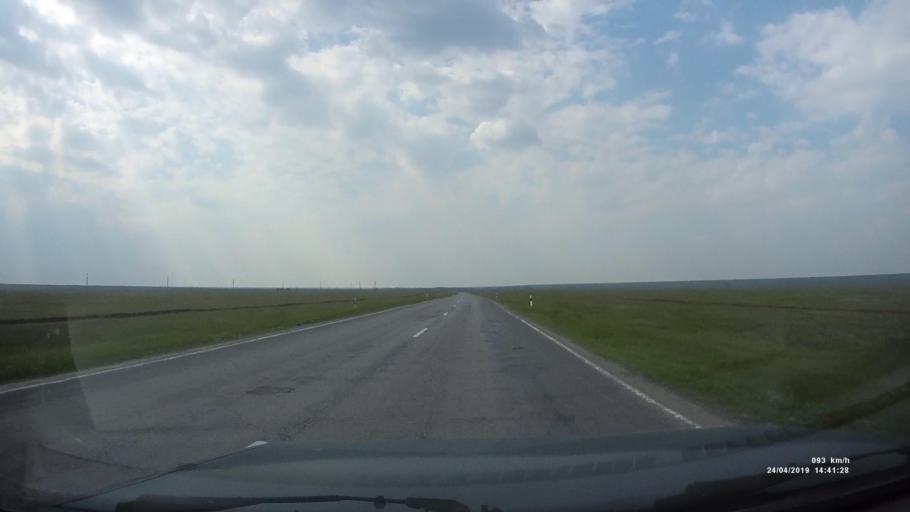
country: RU
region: Rostov
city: Remontnoye
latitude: 46.4455
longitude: 43.8791
